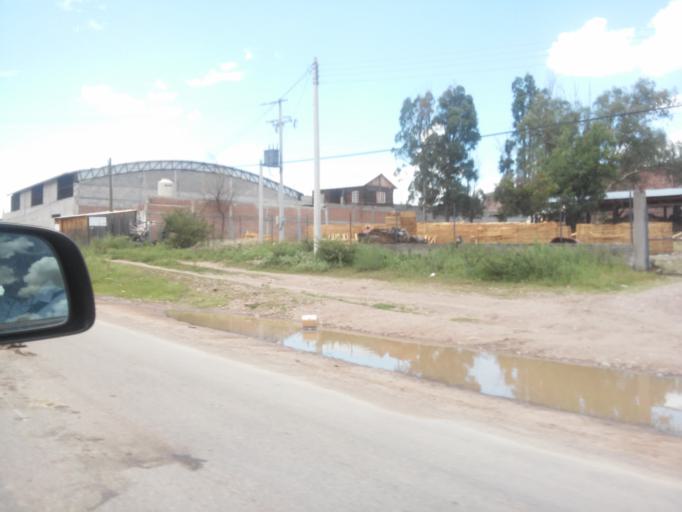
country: MX
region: Durango
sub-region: Santiago Papasquiaro
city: Santiago Papasquiaro
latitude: 25.0754
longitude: -105.4303
